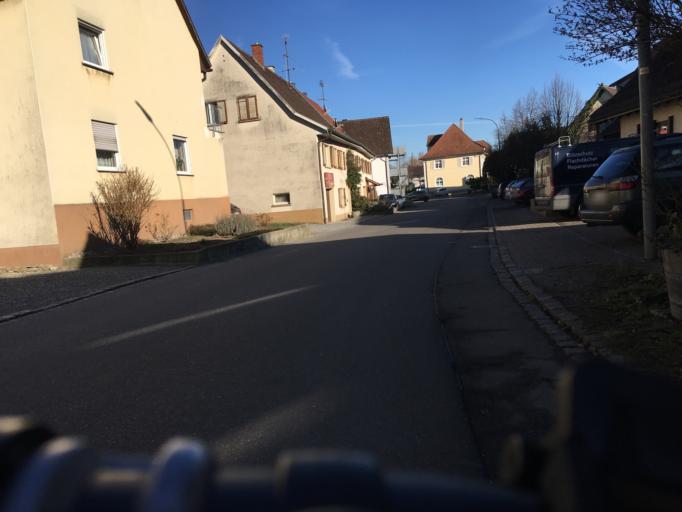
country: DE
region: Baden-Wuerttemberg
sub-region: Freiburg Region
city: Moos
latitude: 47.7186
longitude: 8.8941
